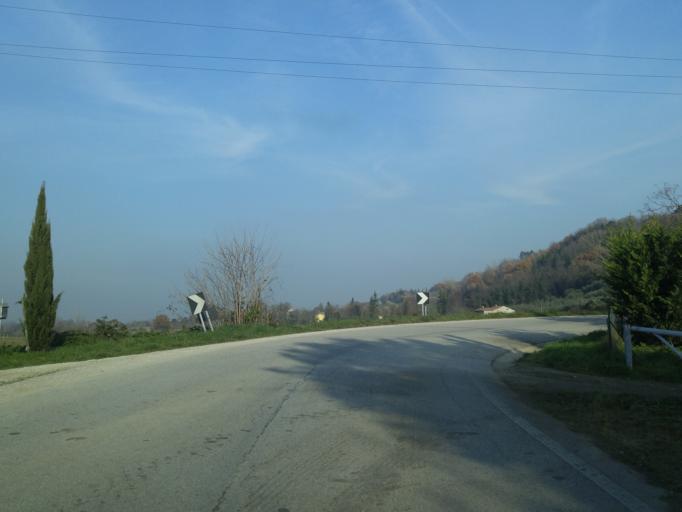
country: IT
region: The Marches
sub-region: Provincia di Pesaro e Urbino
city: Villanova
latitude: 43.7230
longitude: 12.9162
